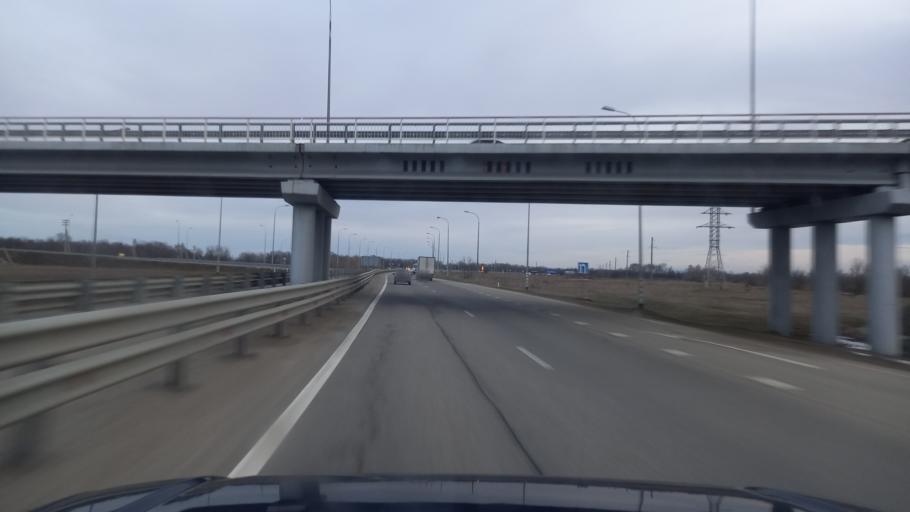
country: RU
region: Adygeya
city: Khanskaya
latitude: 44.6855
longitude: 39.9828
